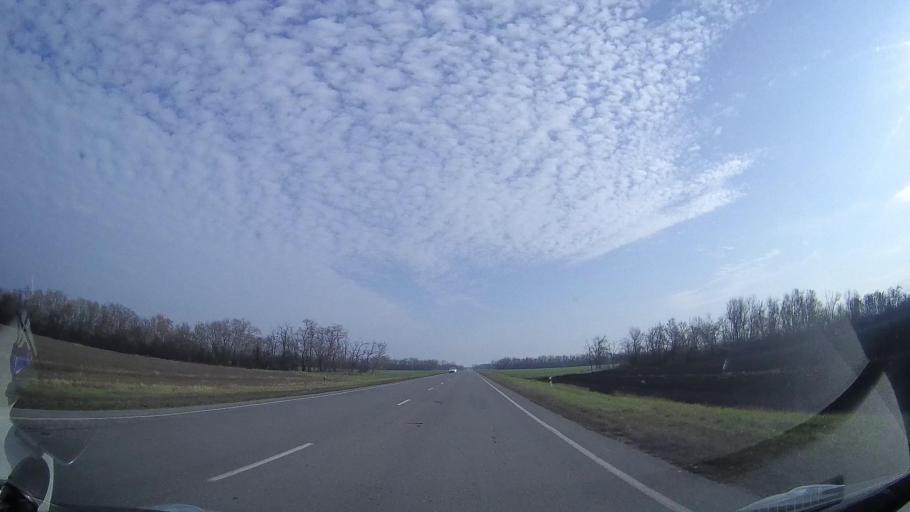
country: RU
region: Rostov
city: Tselina
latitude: 46.5244
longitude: 41.1087
